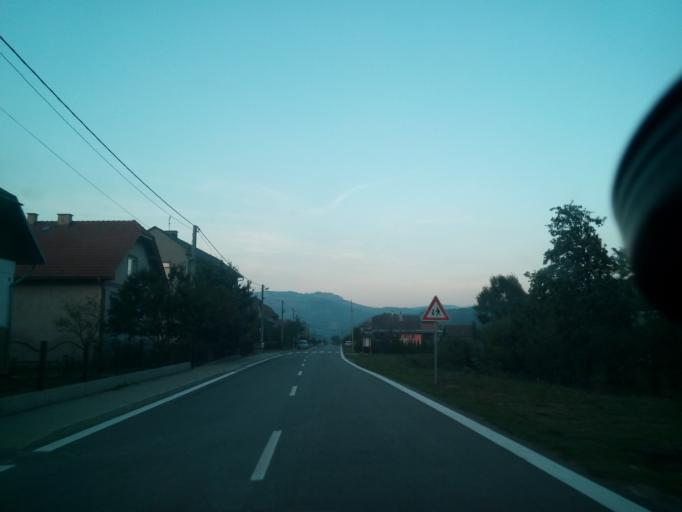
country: SK
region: Kosicky
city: Dobsina
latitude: 48.7867
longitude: 20.3204
